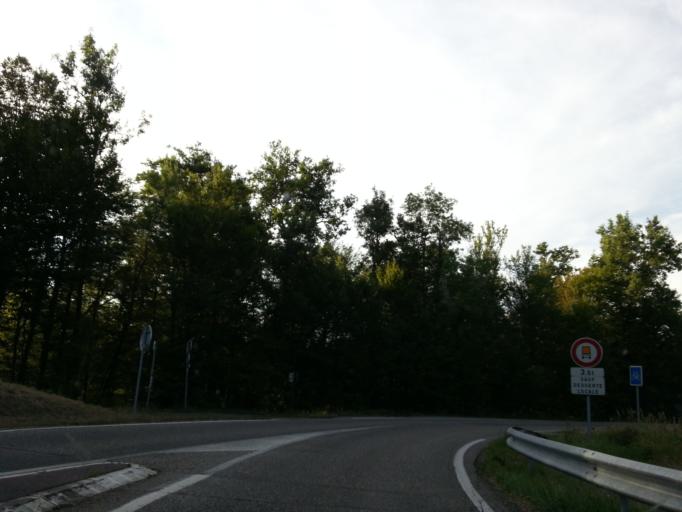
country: FR
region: Alsace
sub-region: Departement du Bas-Rhin
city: Surbourg
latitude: 48.8915
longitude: 7.8330
